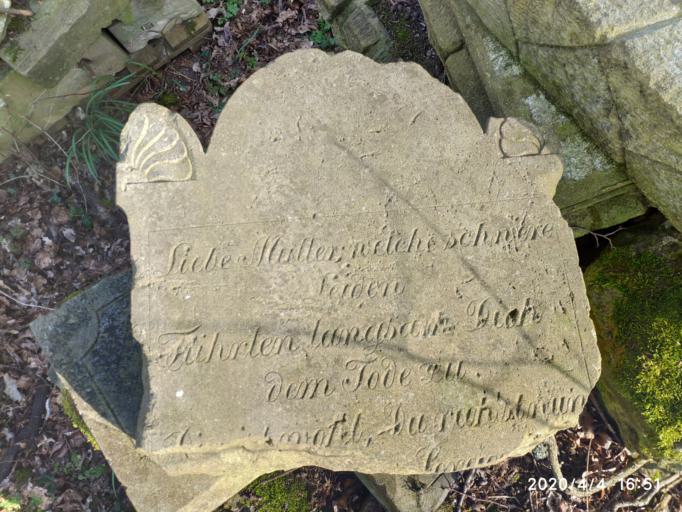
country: PL
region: Lubusz
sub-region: Powiat zielonogorski
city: Swidnica
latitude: 51.8940
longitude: 15.2835
